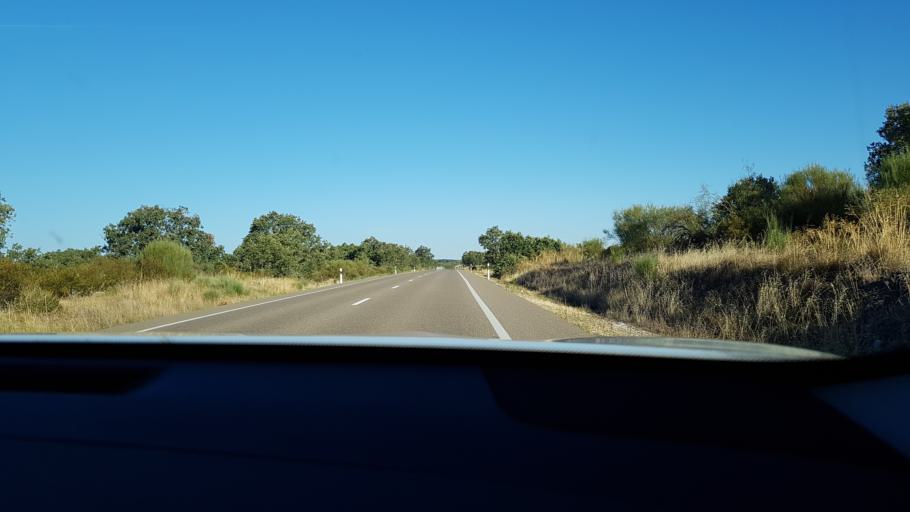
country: ES
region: Castille and Leon
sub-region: Provincia de Zamora
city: Samir de los Canos
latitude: 41.6612
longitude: -6.2036
